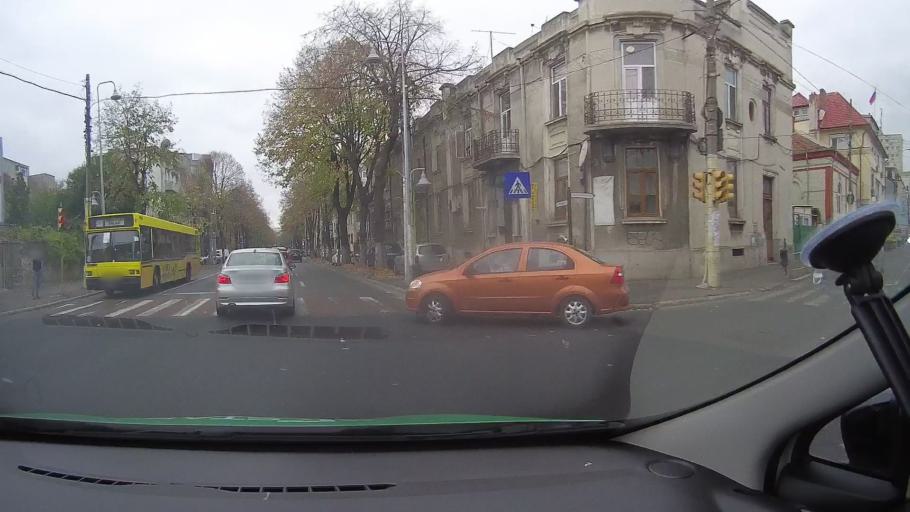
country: RO
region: Constanta
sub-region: Municipiul Constanta
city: Constanta
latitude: 44.1768
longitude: 28.6483
